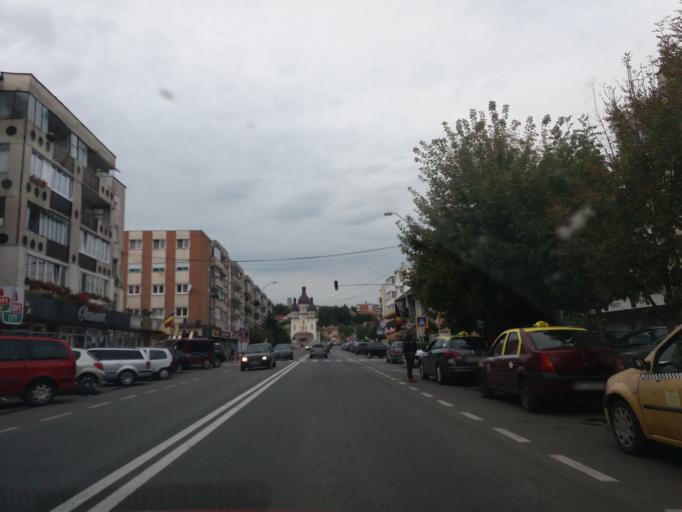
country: RO
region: Mures
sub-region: Municipiul Reghin
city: Reghin
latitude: 46.7727
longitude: 24.7028
